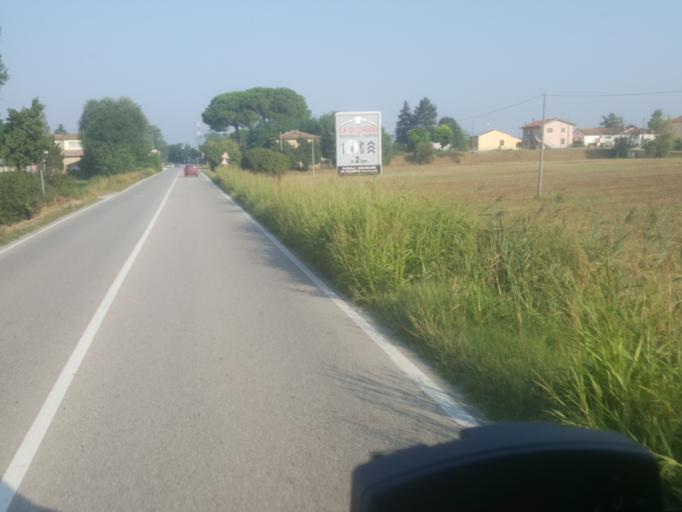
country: IT
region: Emilia-Romagna
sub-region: Provincia di Ravenna
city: Fornace Zarattini
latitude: 44.4426
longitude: 12.1354
